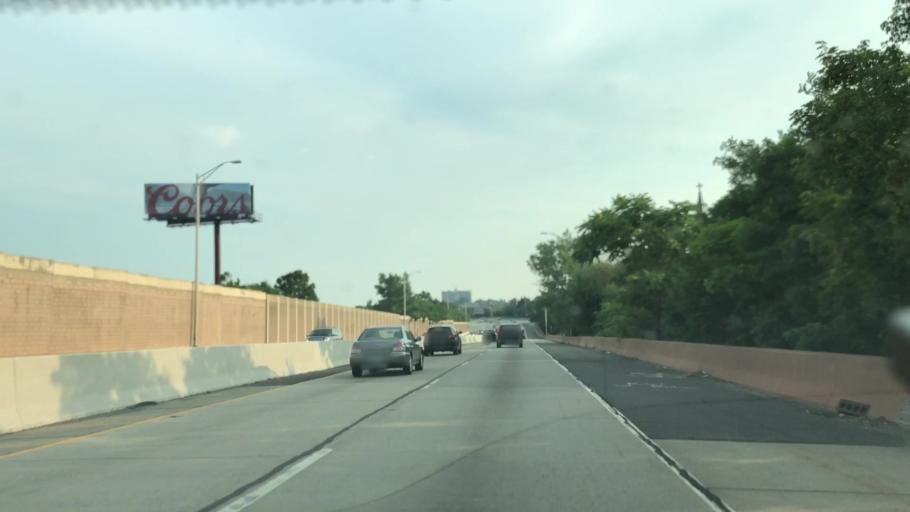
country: US
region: New Jersey
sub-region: Bergen County
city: Garfield
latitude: 40.8689
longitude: -74.1186
